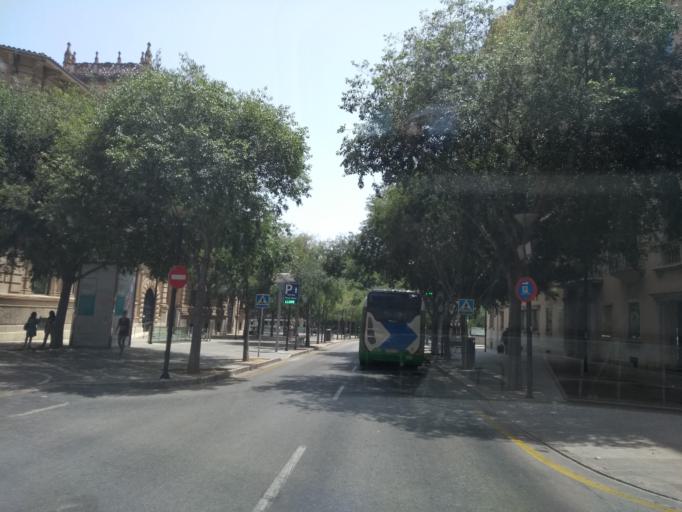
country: ES
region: Balearic Islands
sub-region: Illes Balears
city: Palma
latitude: 39.5760
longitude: 2.6470
